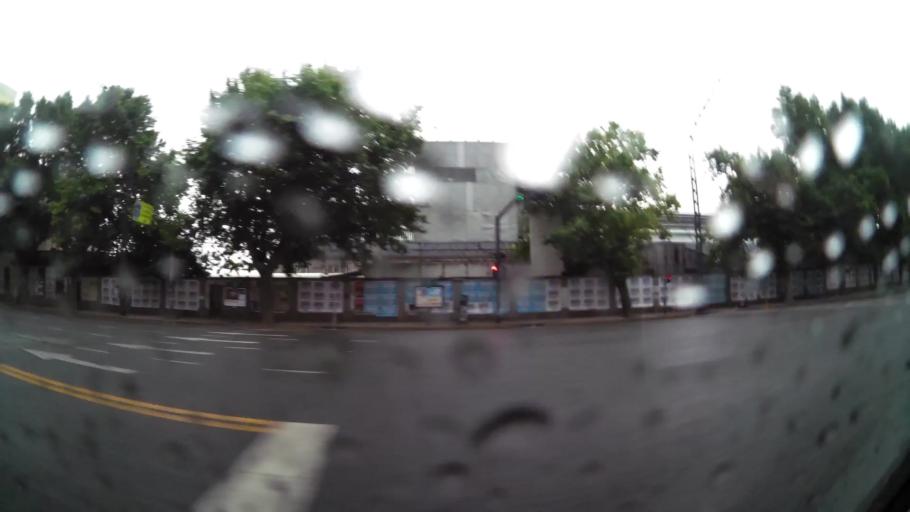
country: AR
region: Buenos Aires F.D.
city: Retiro
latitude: -34.5910
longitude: -58.3778
